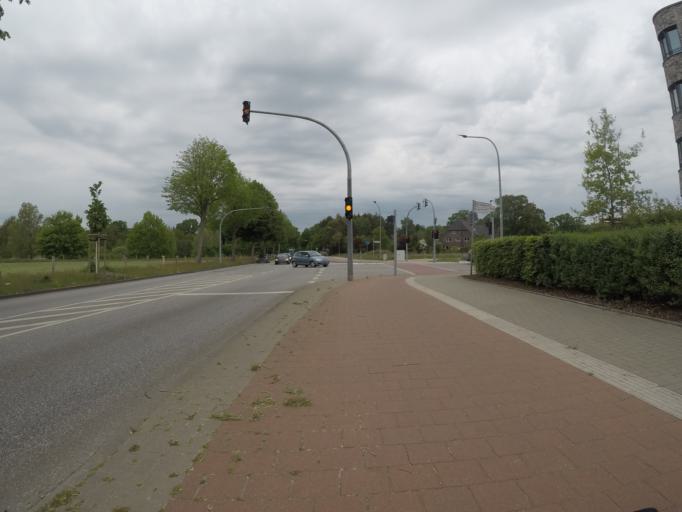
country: DE
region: Schleswig-Holstein
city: Norderstedt
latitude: 53.6957
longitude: 9.9769
